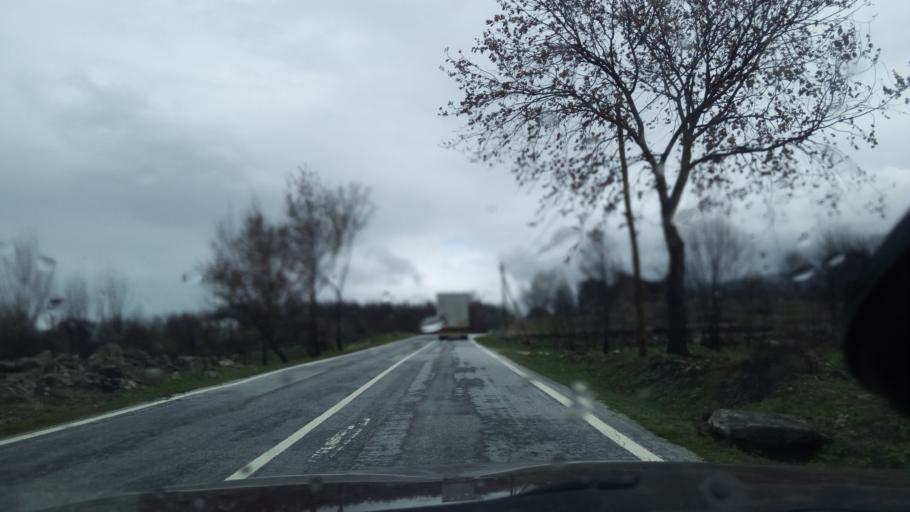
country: PT
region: Guarda
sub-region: Fornos de Algodres
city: Fornos de Algodres
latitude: 40.5560
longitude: -7.5012
